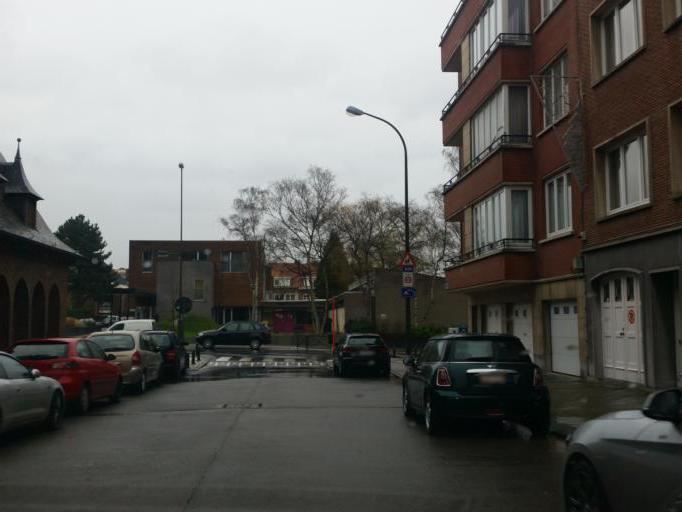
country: BE
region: Brussels Capital
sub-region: Bruxelles-Capitale
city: Brussels
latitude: 50.8099
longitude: 4.3900
